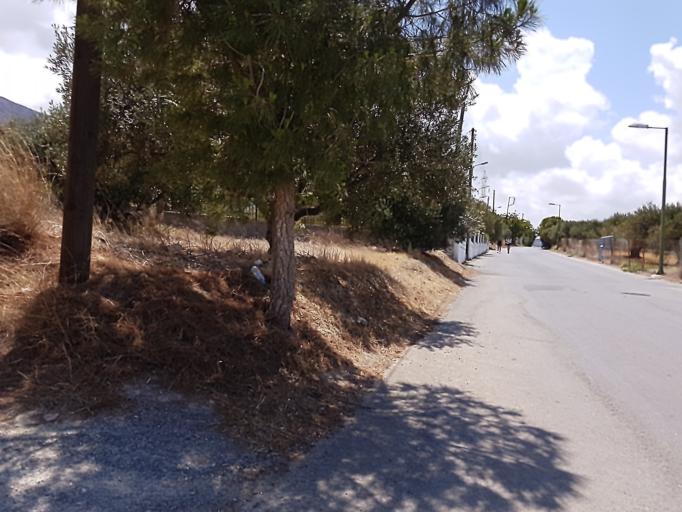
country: GR
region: Crete
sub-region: Nomos Irakleiou
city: Limin Khersonisou
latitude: 35.3158
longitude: 25.3818
